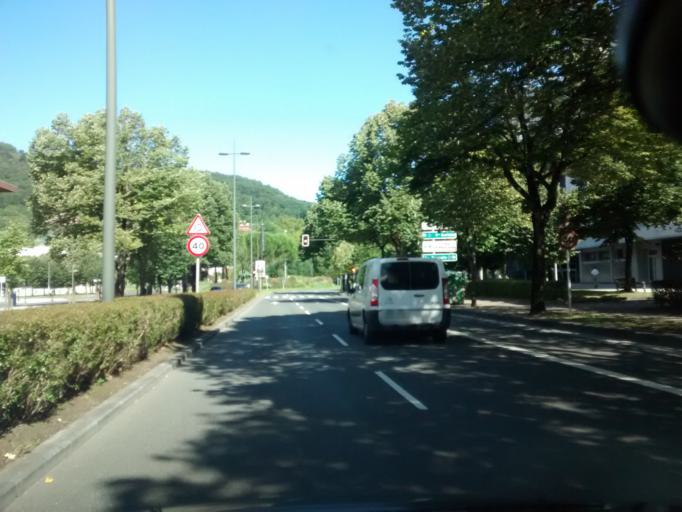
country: ES
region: Basque Country
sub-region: Provincia de Guipuzcoa
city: San Sebastian
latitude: 43.3077
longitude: -2.0089
